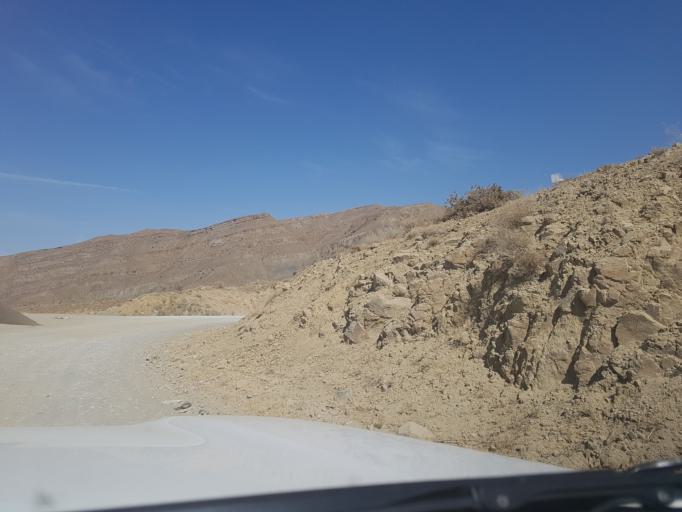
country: TM
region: Ahal
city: Baharly
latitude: 38.4448
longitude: 57.0433
